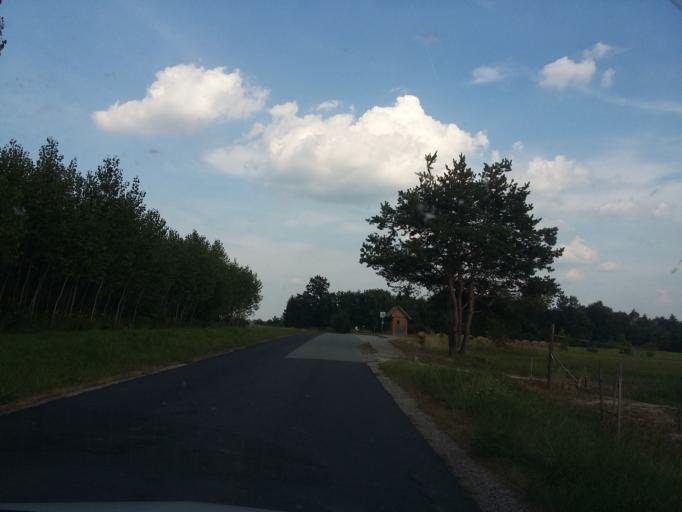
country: SI
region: Hodos-Hodos
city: Hodos
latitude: 46.8499
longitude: 16.3951
